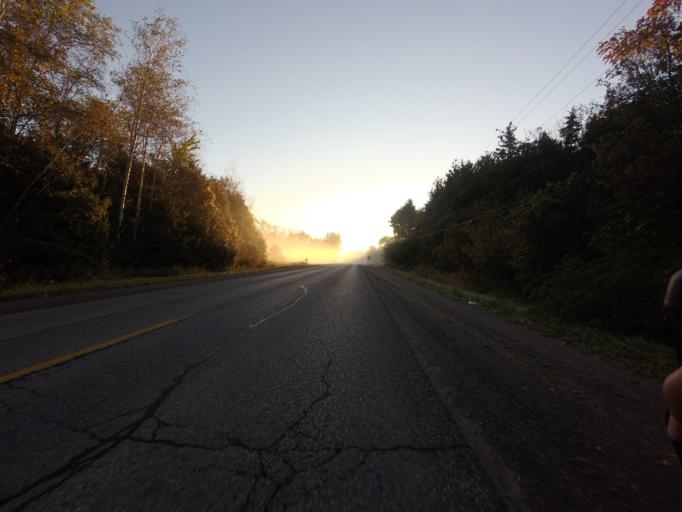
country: CA
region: Ontario
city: Quinte West
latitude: 44.0403
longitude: -77.6090
